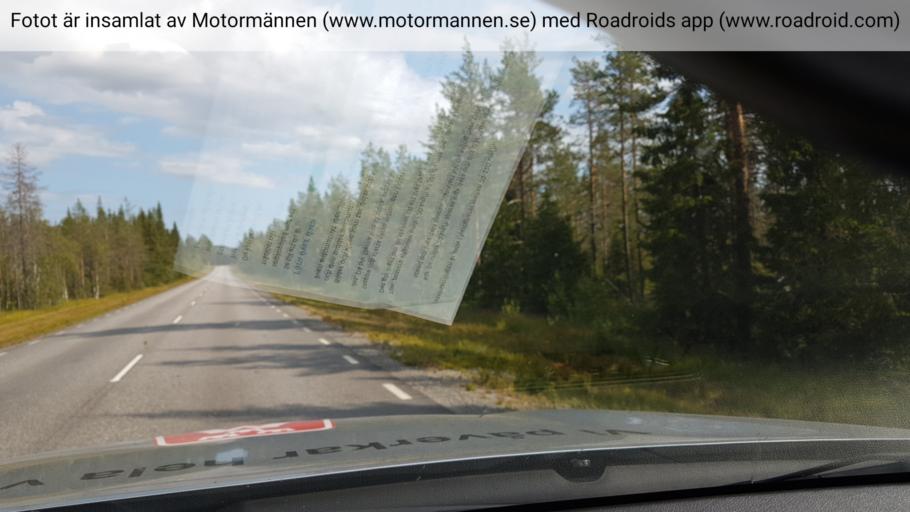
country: SE
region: Vaesterbotten
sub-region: Skelleftea Kommun
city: Storvik
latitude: 65.3375
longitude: 20.5453
